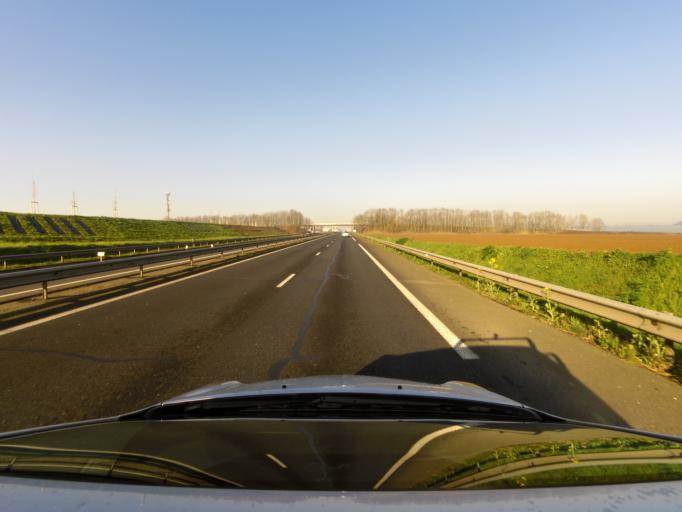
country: FR
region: Lower Normandy
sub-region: Departement du Calvados
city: Verson
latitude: 49.1622
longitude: -0.4496
